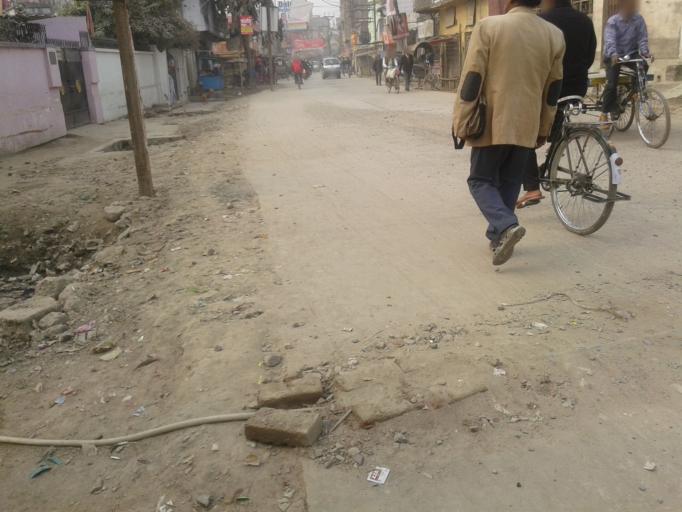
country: IN
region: Bihar
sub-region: Muzaffarpur
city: Muzaffarpur
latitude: 26.1120
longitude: 85.3824
